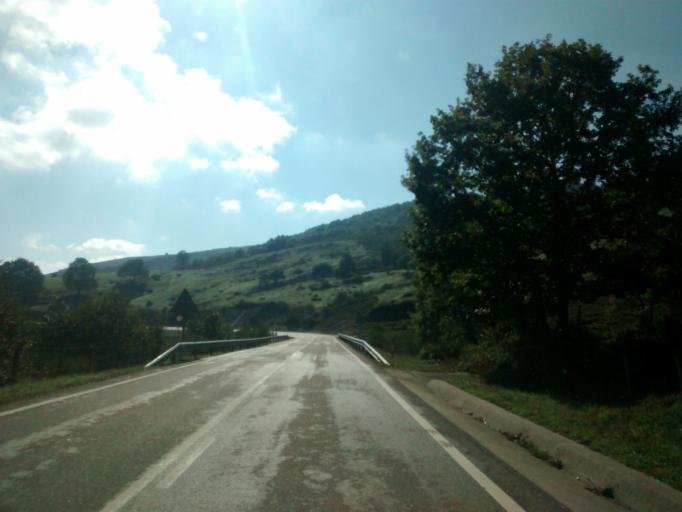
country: ES
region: Cantabria
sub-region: Provincia de Cantabria
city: Reinosa
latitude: 42.9727
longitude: -4.0835
